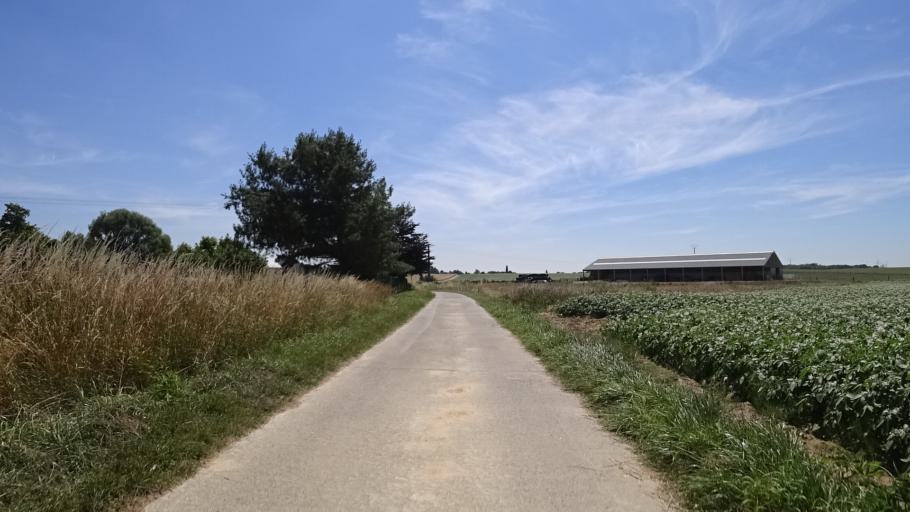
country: BE
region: Wallonia
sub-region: Province de Namur
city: Gembloux
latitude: 50.5765
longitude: 4.6789
